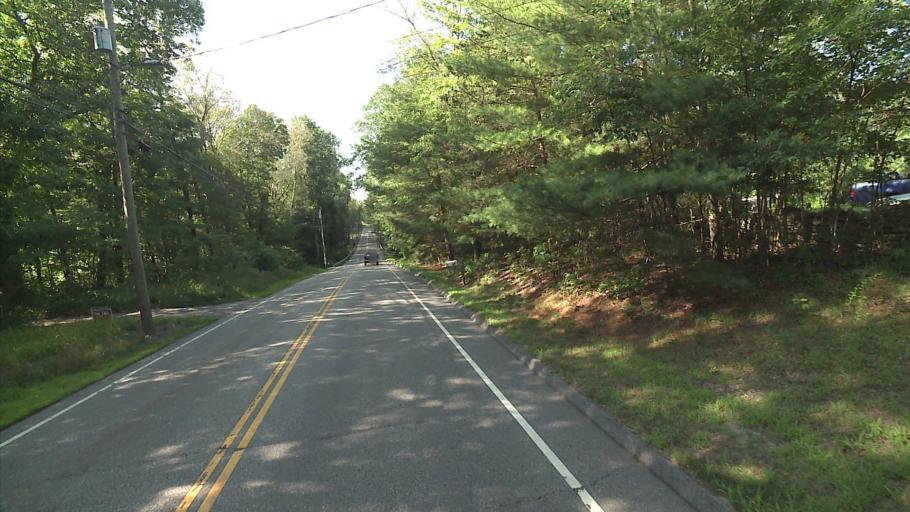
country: US
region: Connecticut
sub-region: New London County
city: Montville Center
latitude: 41.5121
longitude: -72.2030
